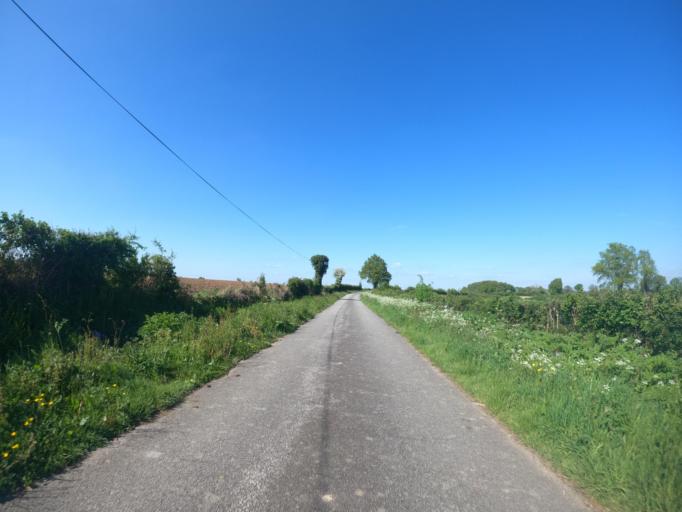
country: FR
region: Poitou-Charentes
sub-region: Departement des Deux-Sevres
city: Moncoutant
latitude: 46.6807
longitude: -0.5297
